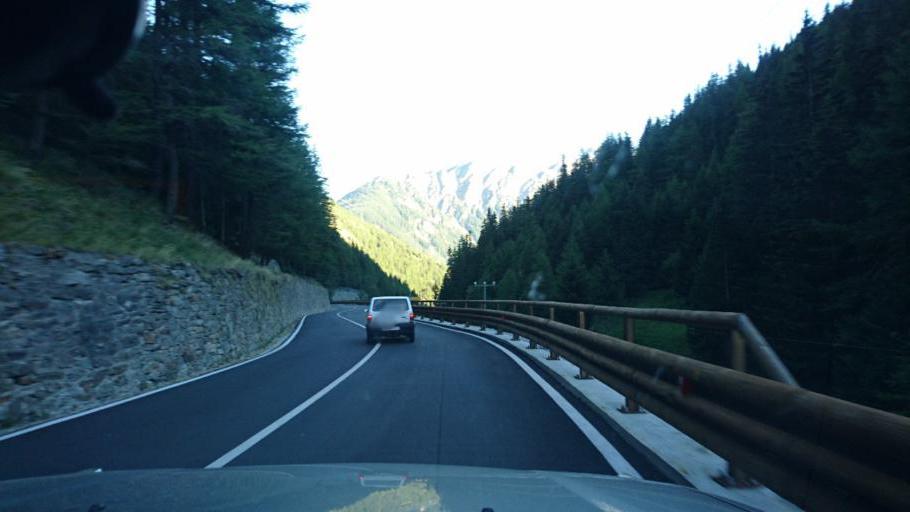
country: IT
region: Aosta Valley
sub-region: Valle d'Aosta
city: San Leonardo
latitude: 45.8403
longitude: 7.1810
